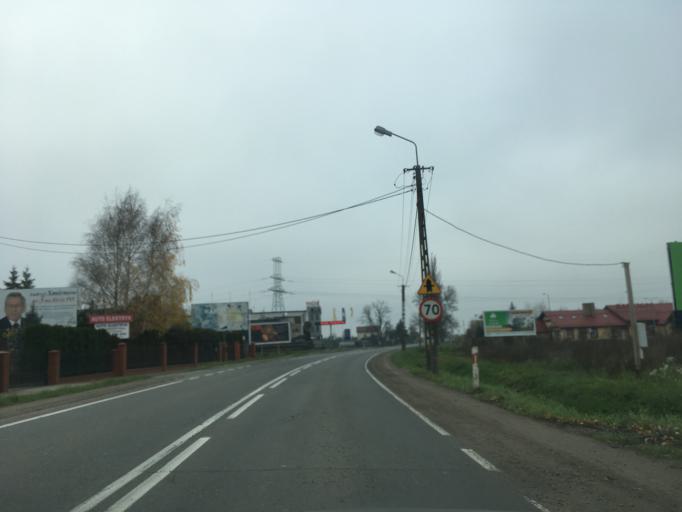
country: PL
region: Masovian Voivodeship
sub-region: Powiat piaseczynski
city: Lesznowola
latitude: 52.0806
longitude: 20.9718
